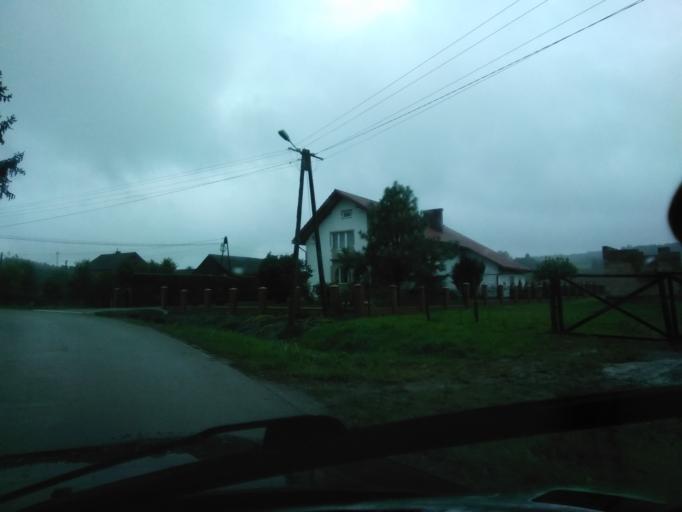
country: PL
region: Subcarpathian Voivodeship
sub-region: Powiat ropczycko-sedziszowski
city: Niedzwiada
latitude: 50.0037
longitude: 21.5502
